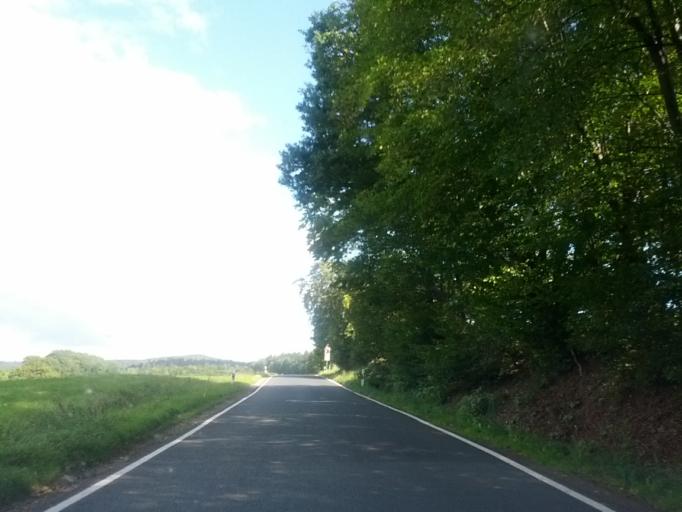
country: DE
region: Thuringia
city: Wolfsburg-Unkeroda
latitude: 50.8957
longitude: 10.3041
